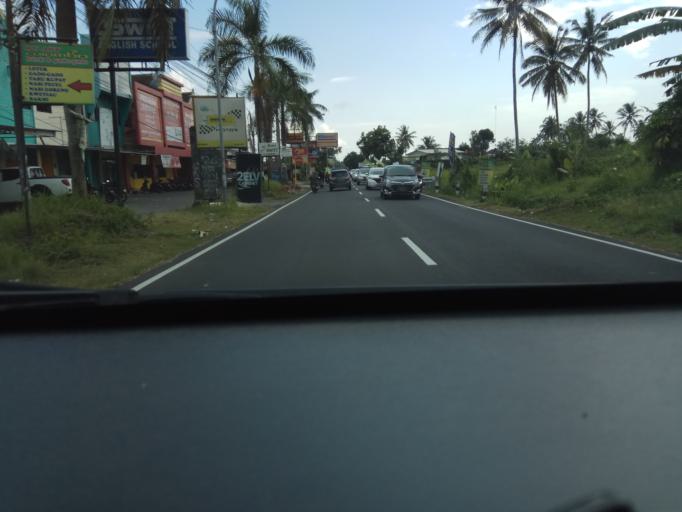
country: ID
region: Daerah Istimewa Yogyakarta
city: Melati
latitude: -7.7084
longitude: 110.4104
